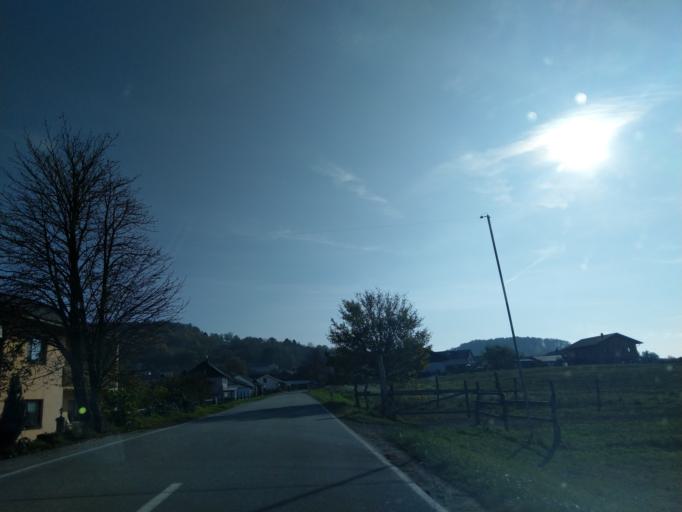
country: DE
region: Bavaria
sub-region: Lower Bavaria
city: Grattersdorf
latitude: 48.8067
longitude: 13.1473
